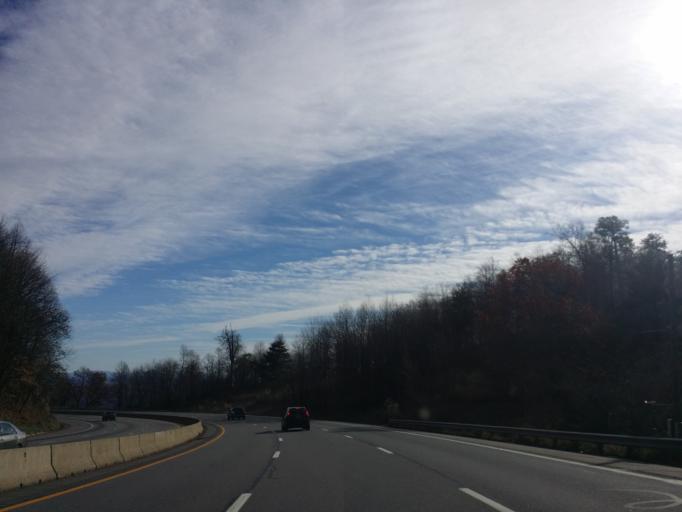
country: US
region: North Carolina
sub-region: Buncombe County
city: Black Mountain
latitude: 35.6162
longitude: -82.2472
